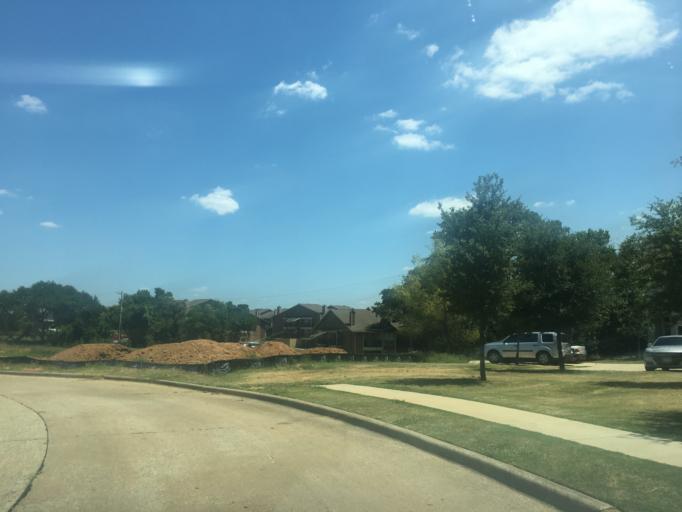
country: US
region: Texas
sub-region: Denton County
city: Lewisville
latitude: 33.0218
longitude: -96.9964
